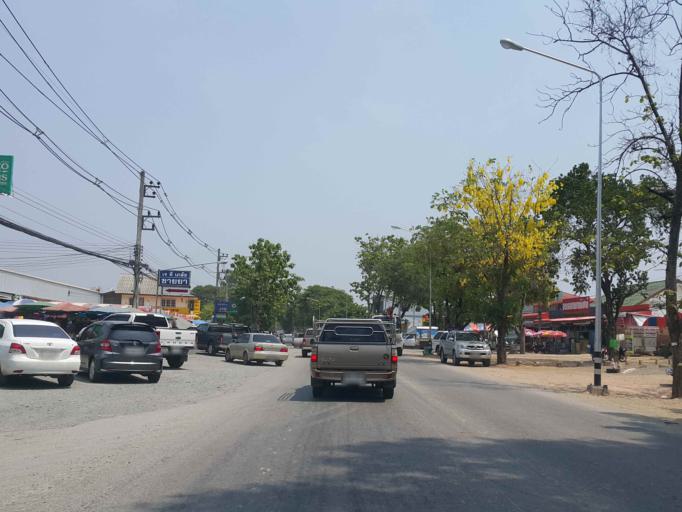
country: TH
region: Chiang Mai
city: San Sai
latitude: 18.9765
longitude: 98.9821
